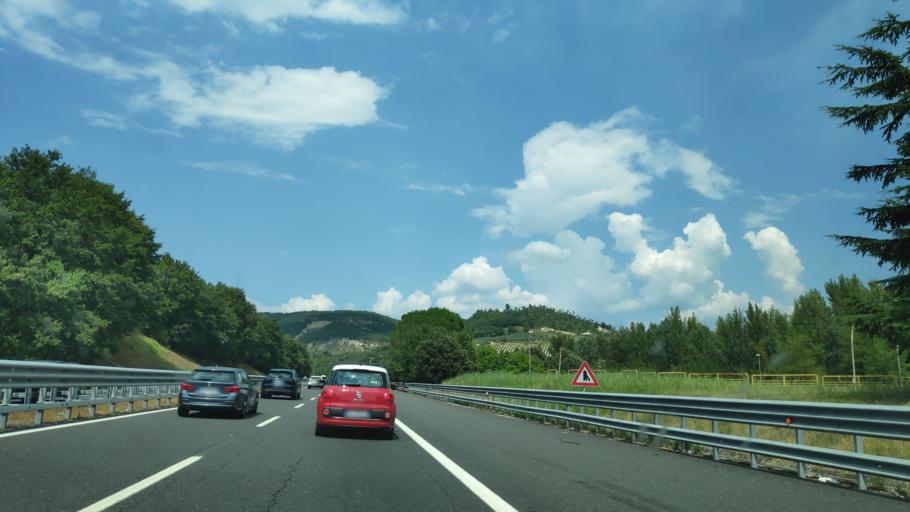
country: IT
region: Umbria
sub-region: Provincia di Terni
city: Stazione di Allerona
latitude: 42.7928
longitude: 12.0476
